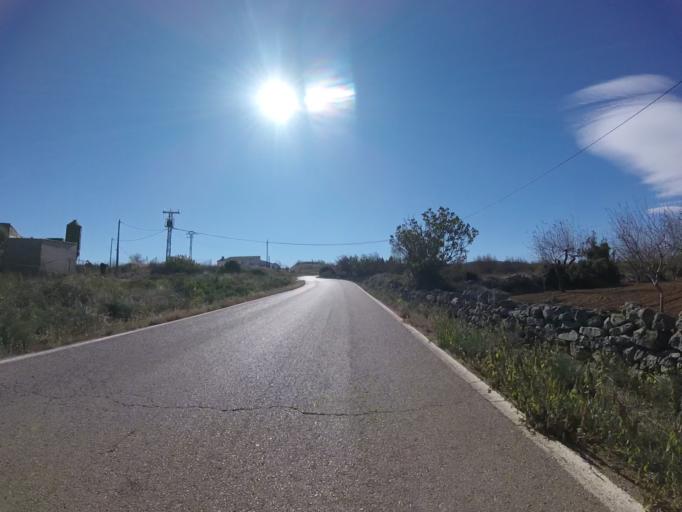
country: ES
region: Valencia
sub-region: Provincia de Castello
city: Albocasser
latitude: 40.3696
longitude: 0.0196
